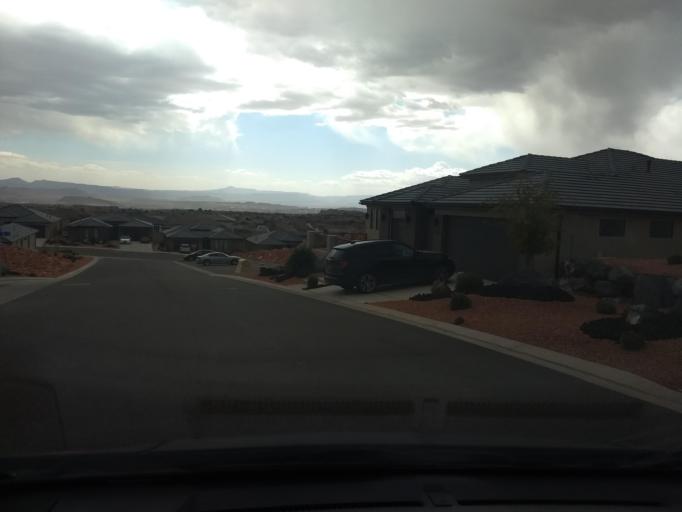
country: US
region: Utah
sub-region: Washington County
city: Washington
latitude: 37.1605
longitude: -113.5253
